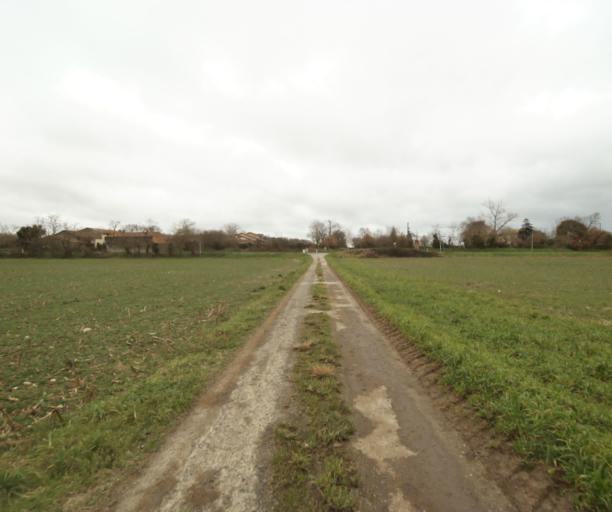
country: FR
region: Midi-Pyrenees
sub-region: Departement de l'Ariege
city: Pamiers
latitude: 43.1838
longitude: 1.6334
